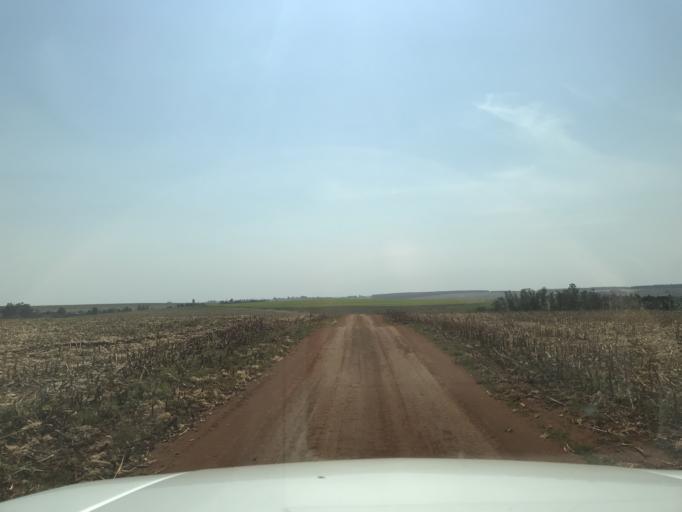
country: BR
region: Parana
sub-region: Palotina
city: Palotina
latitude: -24.2342
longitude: -53.7482
